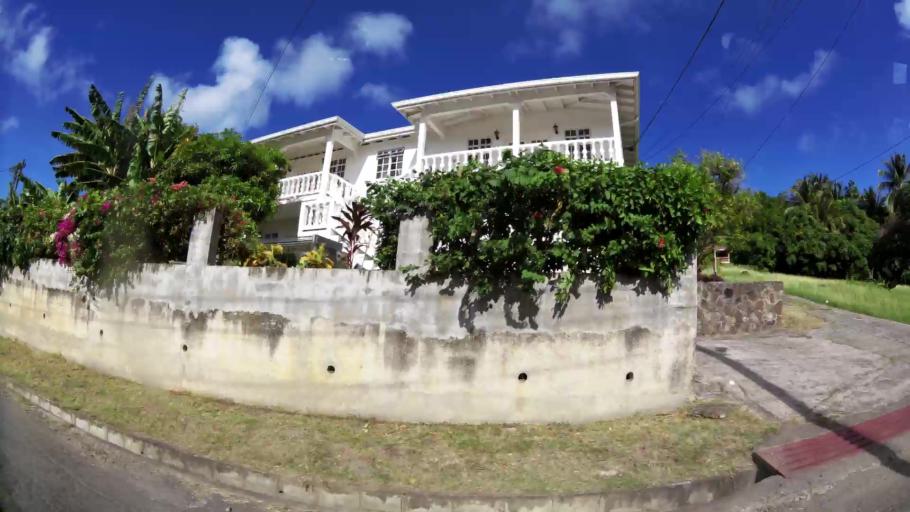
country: LC
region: Gros-Islet
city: Gros Islet
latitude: 14.0493
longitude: -60.9640
